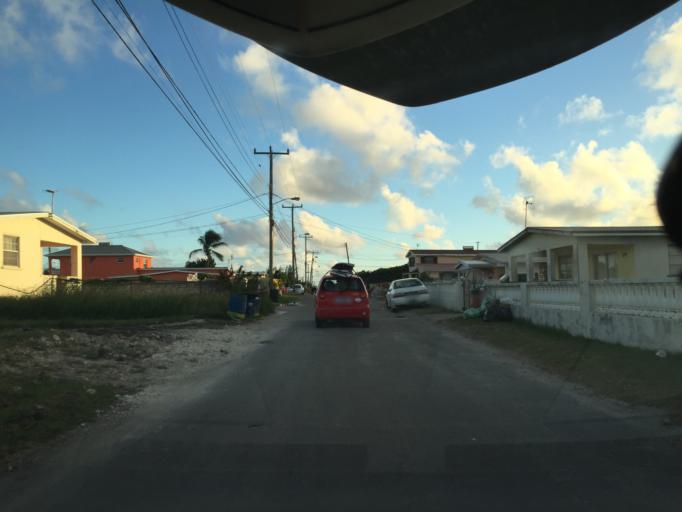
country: BB
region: Christ Church
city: Oistins
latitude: 13.0572
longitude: -59.5110
